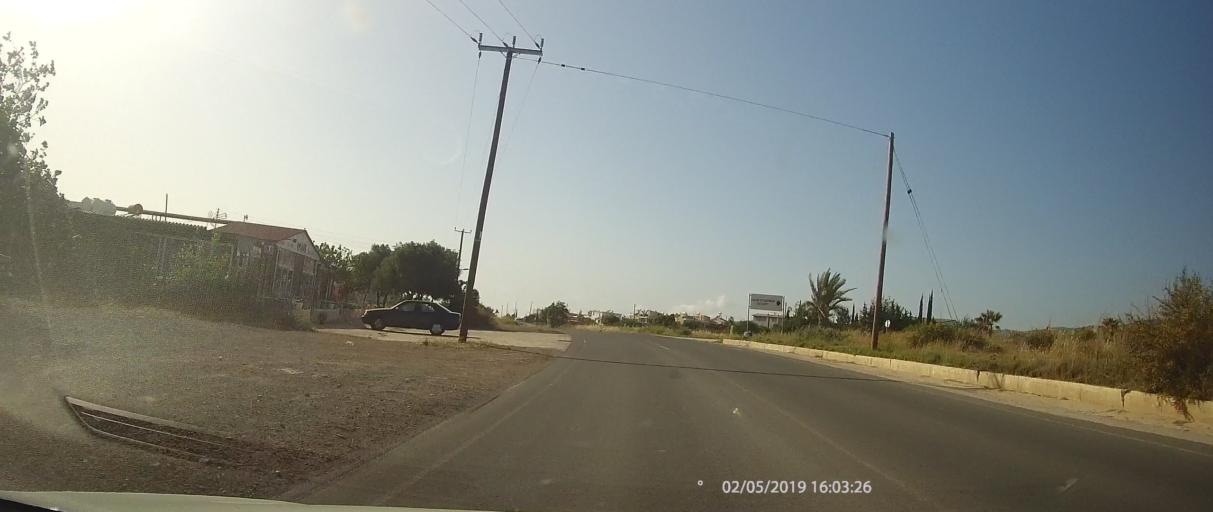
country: CY
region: Pafos
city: Empa
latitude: 34.8159
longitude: 32.4281
